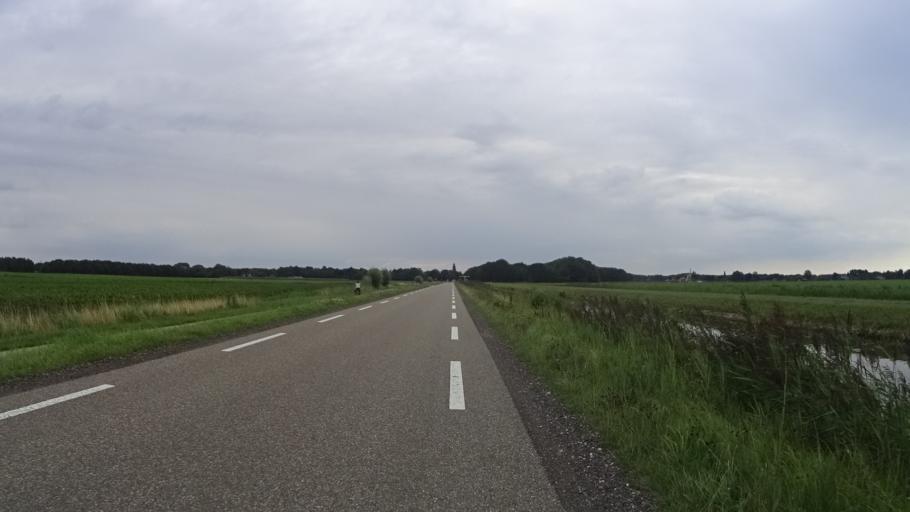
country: NL
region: Groningen
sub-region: Gemeente Slochteren
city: Slochteren
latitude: 53.2254
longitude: 6.7845
